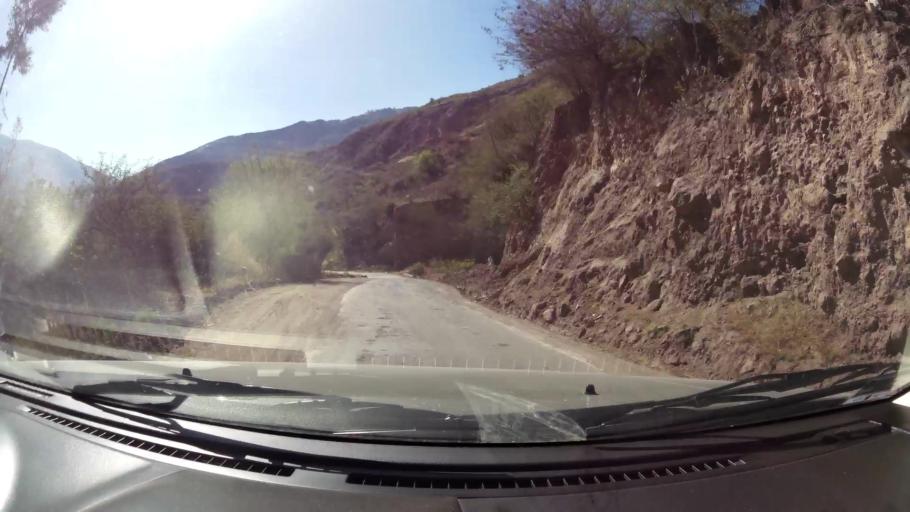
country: PE
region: Huancavelica
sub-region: Provincia de Acobamba
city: Pomacocha
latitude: -12.7713
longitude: -74.4985
